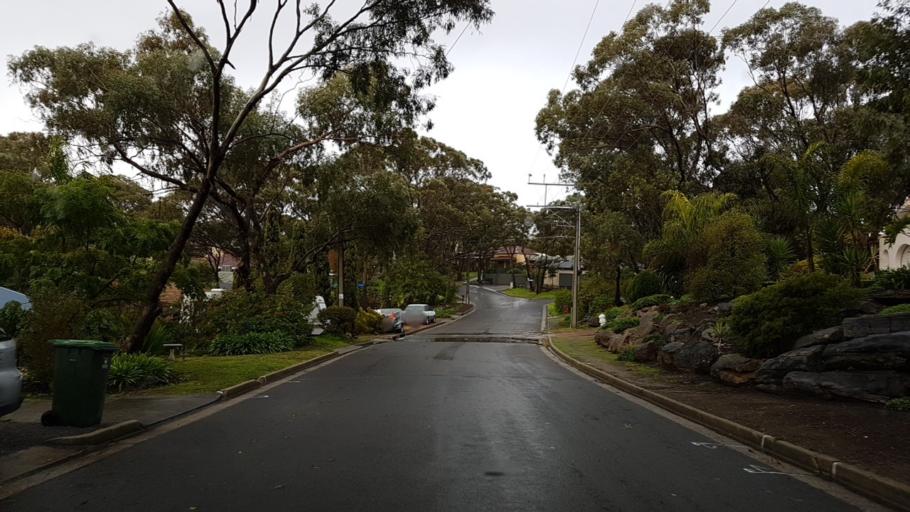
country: AU
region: South Australia
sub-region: Onkaparinga
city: Bedford Park
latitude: -35.0442
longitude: 138.5803
